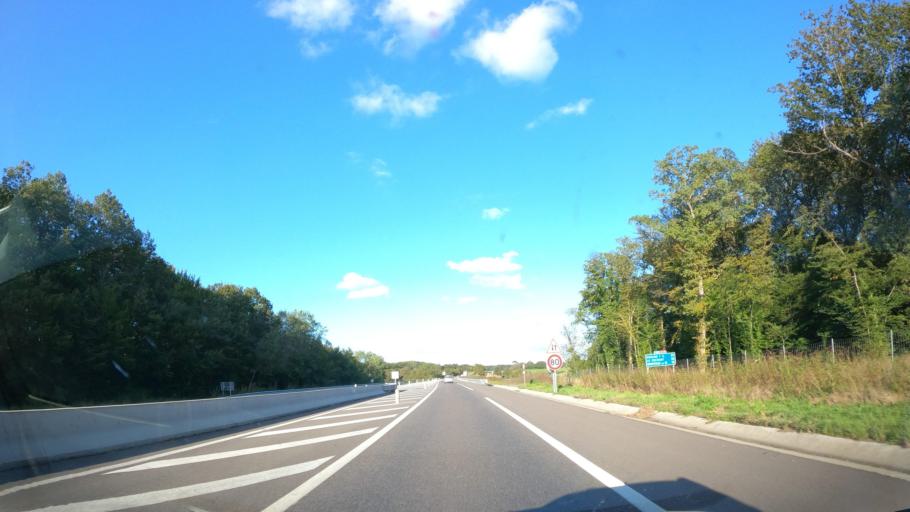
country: FR
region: Bourgogne
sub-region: Departement de Saone-et-Loire
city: Genelard
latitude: 46.5992
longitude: 4.2411
